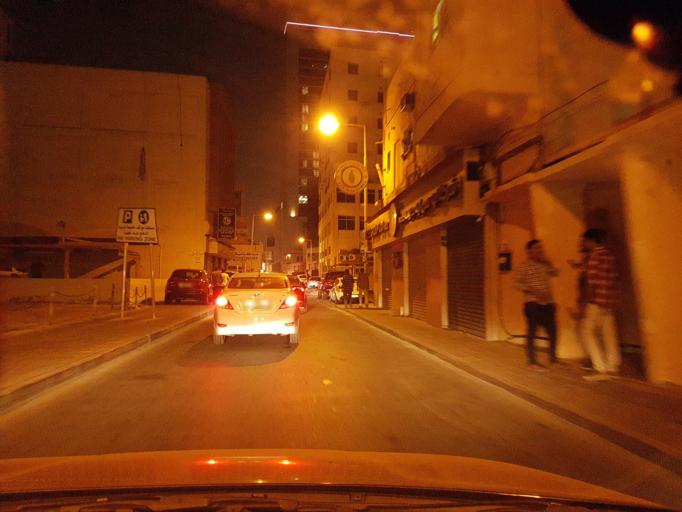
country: BH
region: Manama
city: Manama
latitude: 26.2360
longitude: 50.5791
